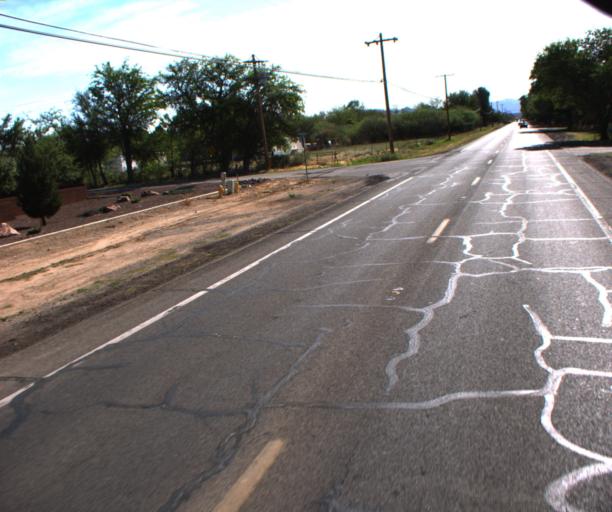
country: US
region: Arizona
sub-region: Cochise County
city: Saint David
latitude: 31.9053
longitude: -110.2356
